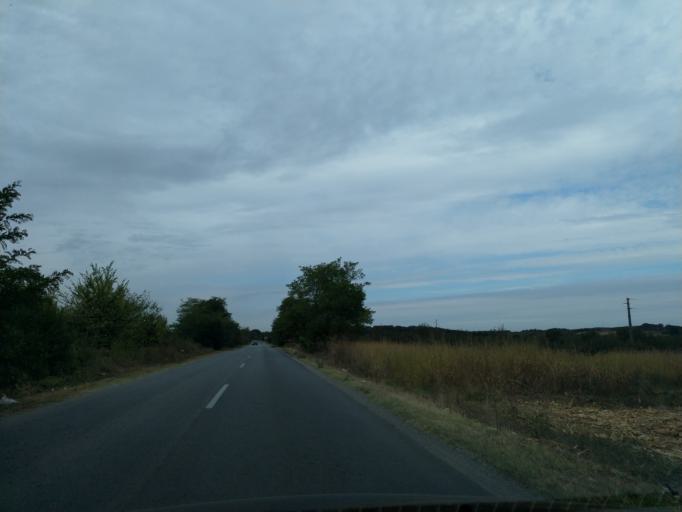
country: RS
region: Central Serbia
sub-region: Pomoravski Okrug
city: Jagodina
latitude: 43.9984
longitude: 21.2173
